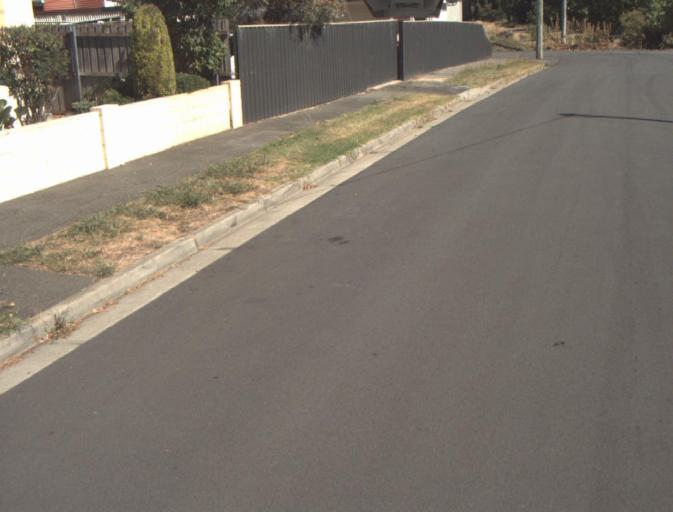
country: AU
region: Tasmania
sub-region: Launceston
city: Newnham
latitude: -41.4143
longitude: 147.1378
